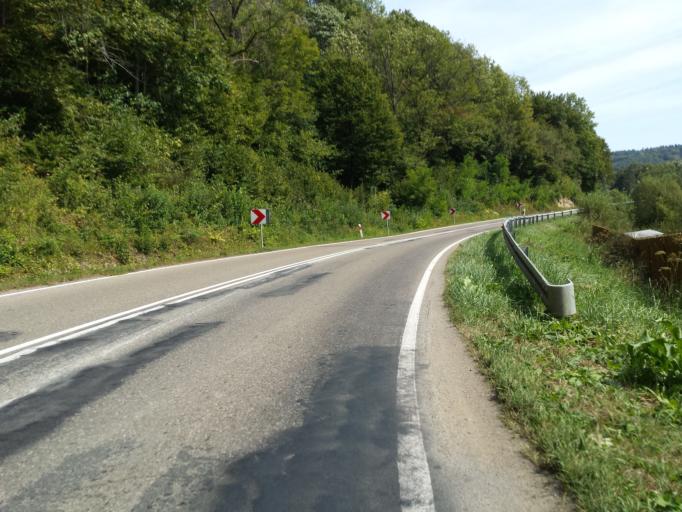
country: PL
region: Subcarpathian Voivodeship
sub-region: Powiat leski
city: Baligrod
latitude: 49.3820
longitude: 22.2787
